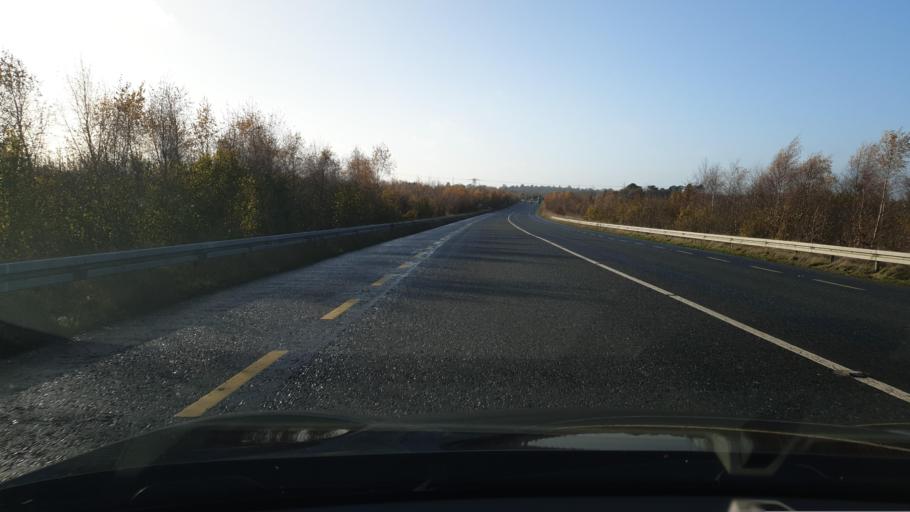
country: IE
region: Leinster
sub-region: An Mhi
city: Dunboyne
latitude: 53.4293
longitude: -6.4802
